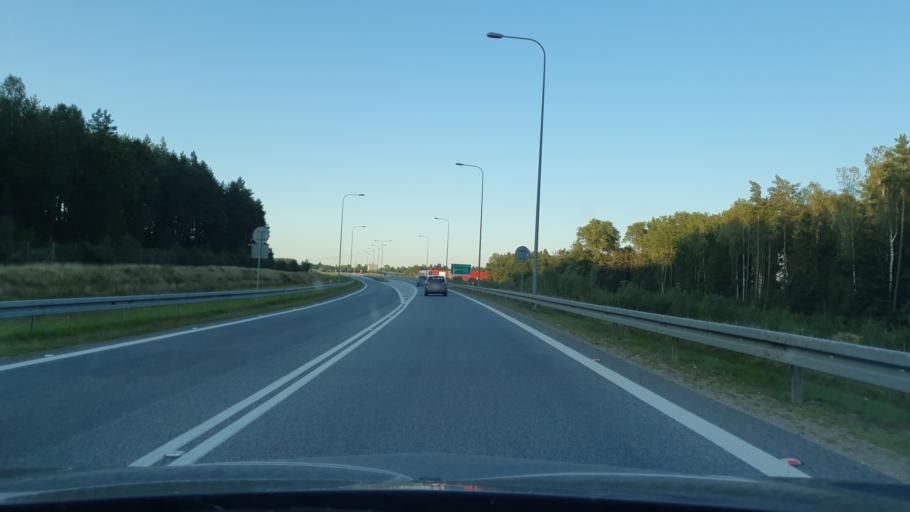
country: PL
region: Pomeranian Voivodeship
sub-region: Slupsk
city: Slupsk
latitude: 54.4427
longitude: 17.0770
